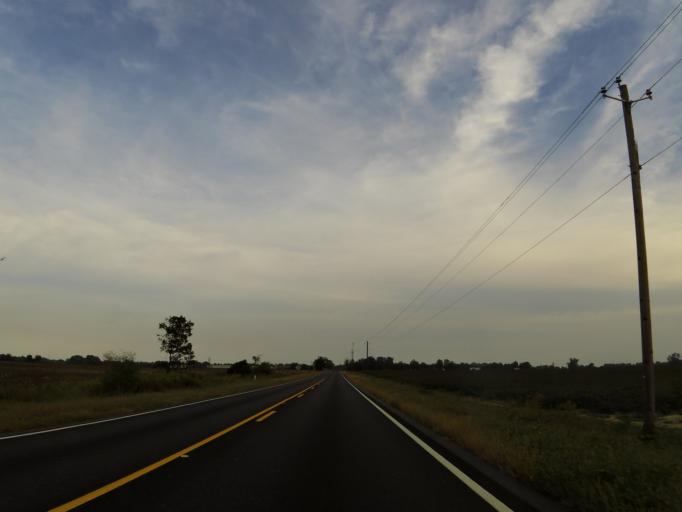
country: US
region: Alabama
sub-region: Escambia County
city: Atmore
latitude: 31.2255
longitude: -87.4770
